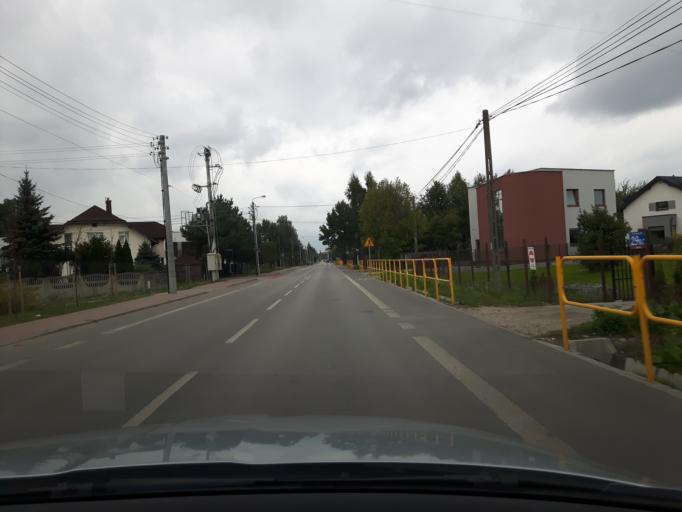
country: PL
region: Masovian Voivodeship
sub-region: Powiat wolominski
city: Kobylka
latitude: 52.3217
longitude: 21.1899
